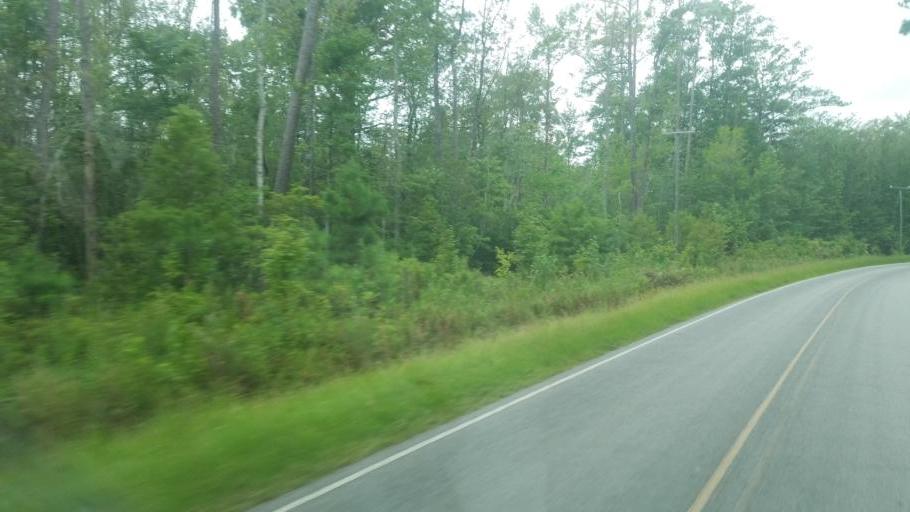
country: US
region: North Carolina
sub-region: Tyrrell County
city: Columbia
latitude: 35.9336
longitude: -76.2646
